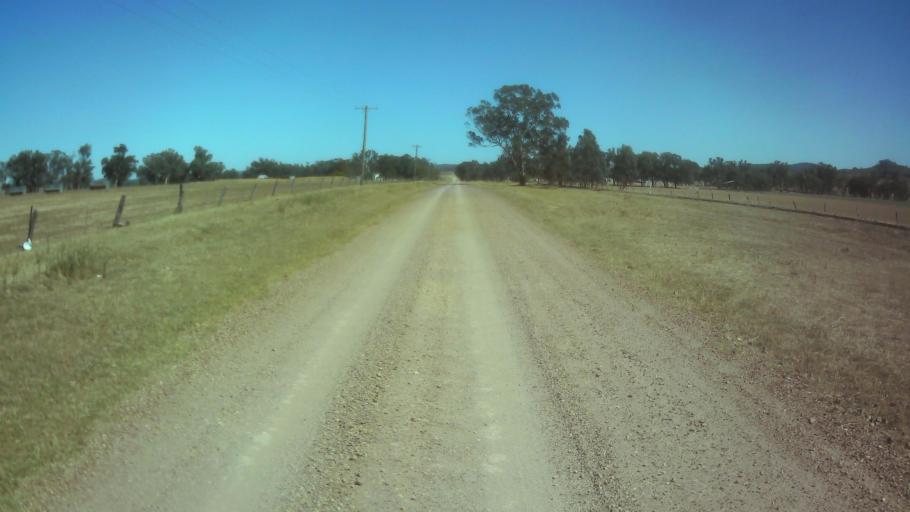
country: AU
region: New South Wales
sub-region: Weddin
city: Grenfell
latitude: -33.9472
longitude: 148.2955
